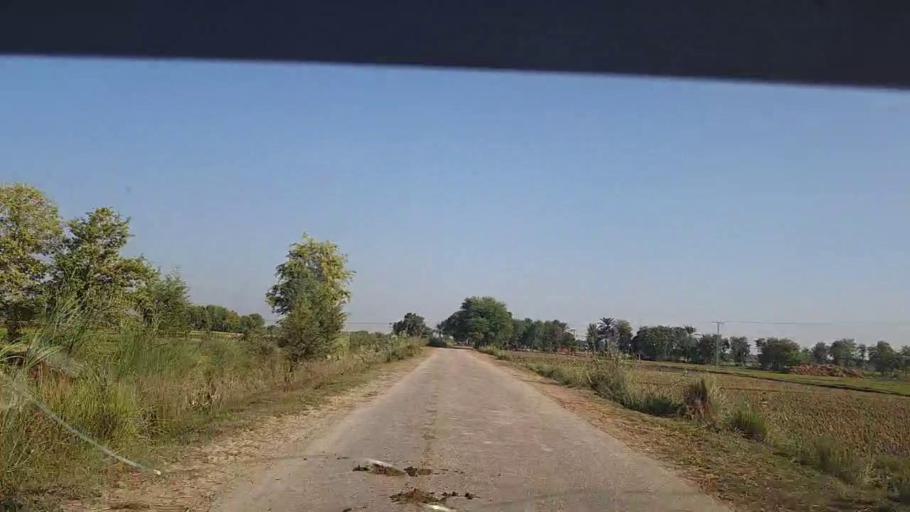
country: PK
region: Sindh
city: Larkana
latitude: 27.6228
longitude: 68.2427
